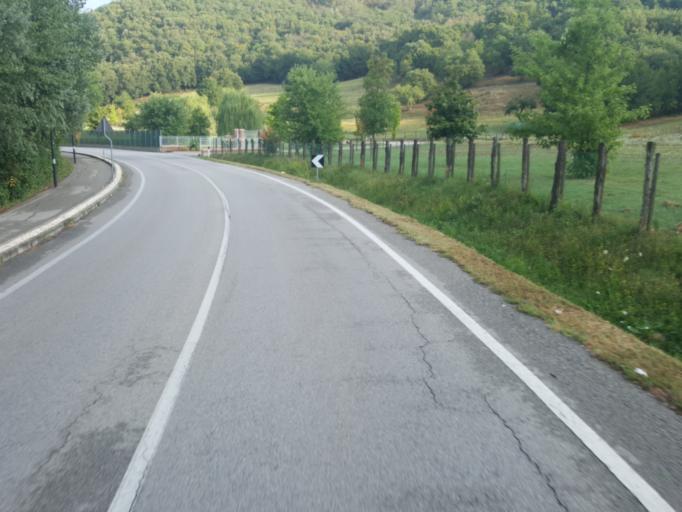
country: IT
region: Veneto
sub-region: Provincia di Padova
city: Battaglia Terme
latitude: 45.2931
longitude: 11.7691
